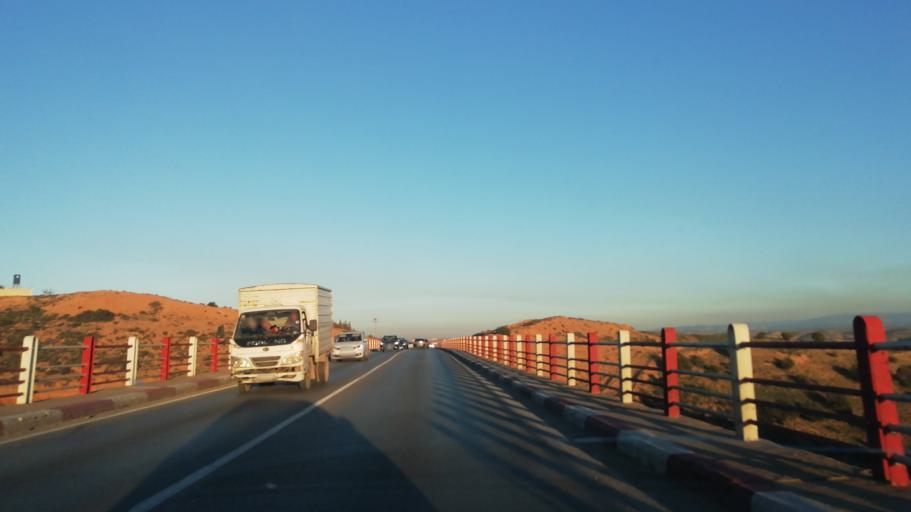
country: DZ
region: Tlemcen
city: Nedroma
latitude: 34.8918
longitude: -1.6652
